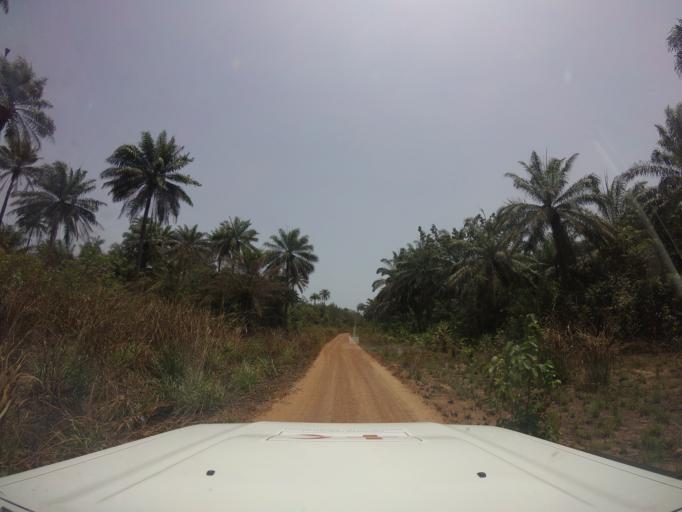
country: LR
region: Grand Cape Mount
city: Robertsport
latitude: 6.9304
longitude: -11.3550
